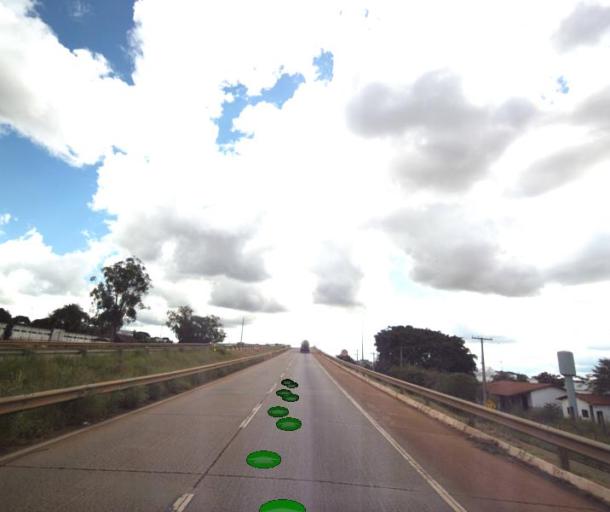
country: BR
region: Goias
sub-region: Anapolis
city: Anapolis
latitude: -16.3536
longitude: -48.9265
